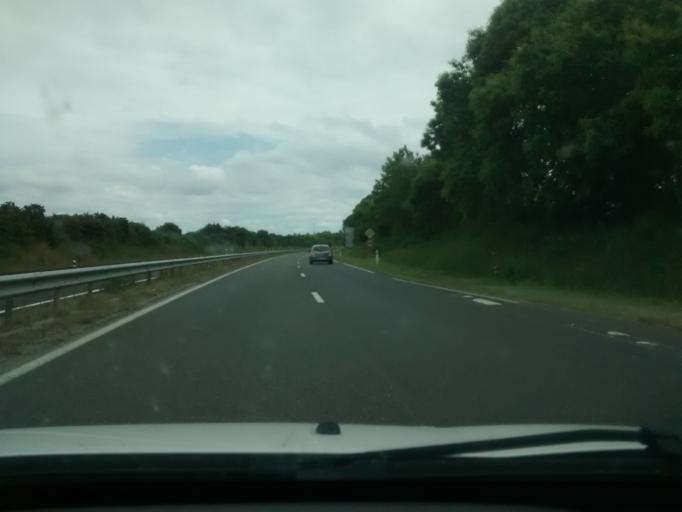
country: FR
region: Brittany
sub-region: Departement des Cotes-d'Armor
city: Cavan
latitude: 48.6805
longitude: -3.3567
